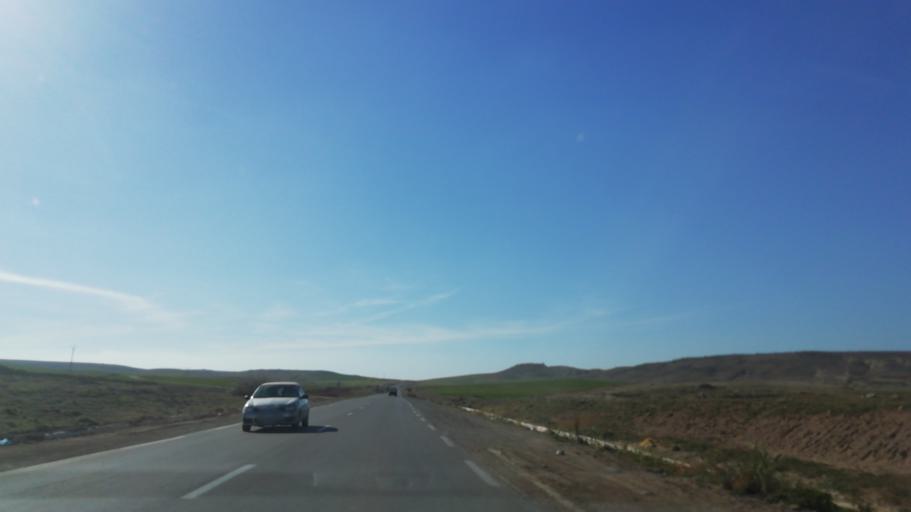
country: DZ
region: Mascara
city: Oued el Abtal
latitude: 35.4461
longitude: 0.5946
